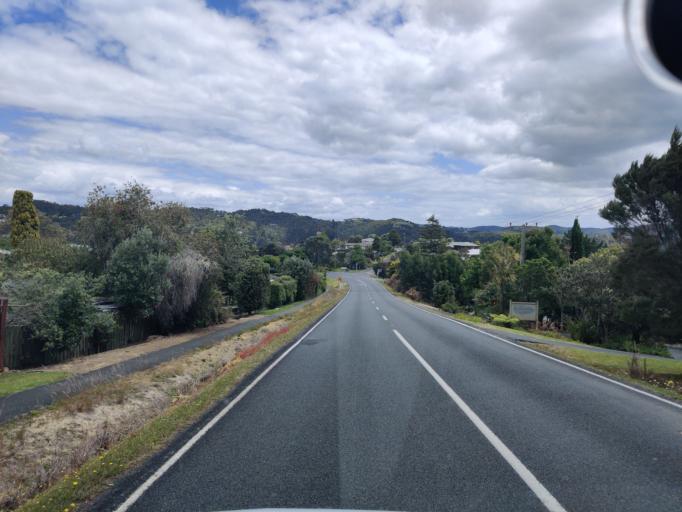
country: NZ
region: Northland
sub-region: Far North District
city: Paihia
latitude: -35.3037
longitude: 174.1238
